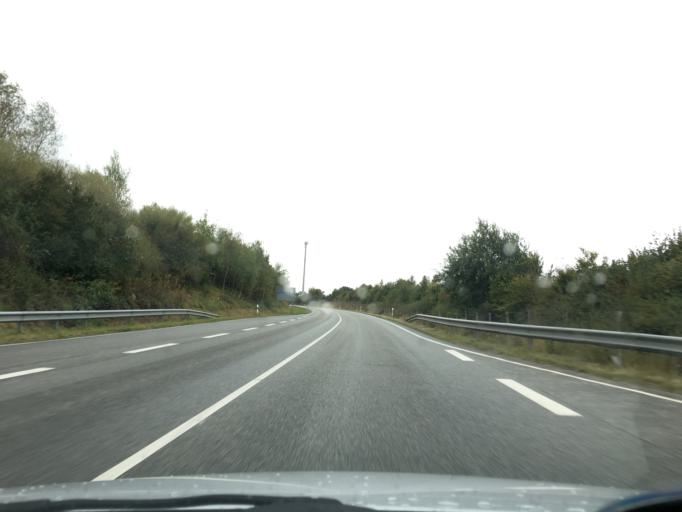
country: DE
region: Schleswig-Holstein
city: Gettorf
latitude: 54.4149
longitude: 9.9889
